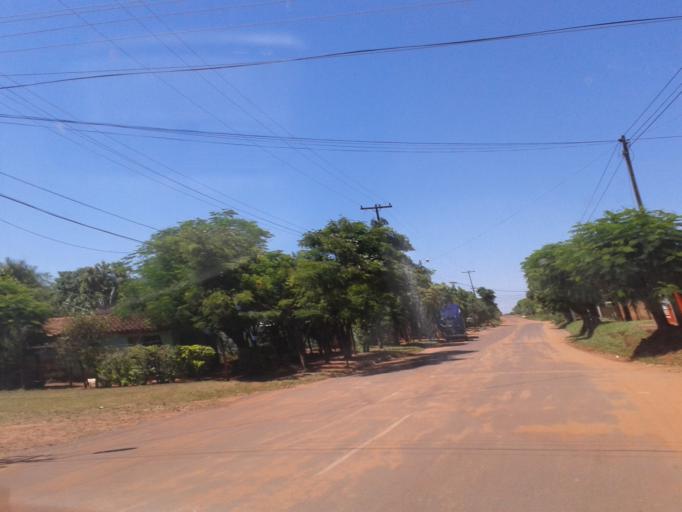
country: PY
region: Misiones
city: Santa Maria
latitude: -26.8973
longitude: -57.0276
